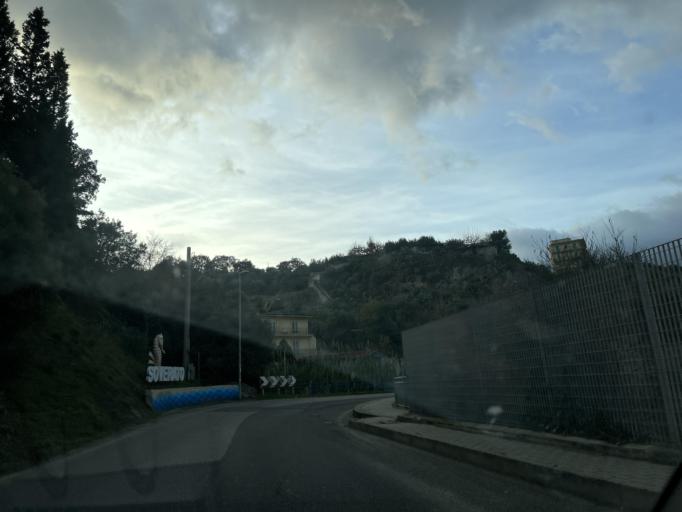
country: IT
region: Calabria
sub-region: Provincia di Catanzaro
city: Soverato Superiore
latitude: 38.6962
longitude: 16.5423
